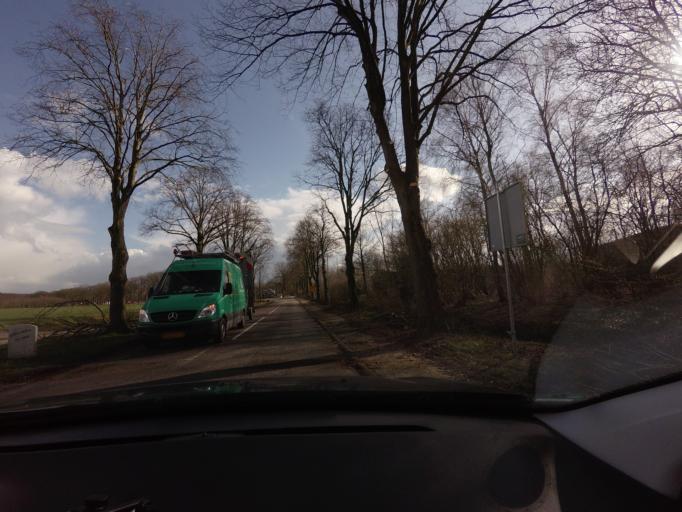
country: NL
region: Drenthe
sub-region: Gemeente Assen
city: Assen
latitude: 52.8446
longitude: 6.6230
